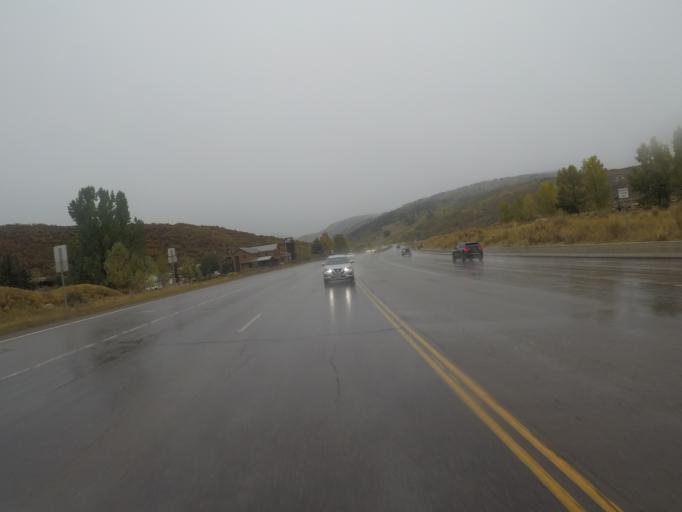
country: US
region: Colorado
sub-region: Pitkin County
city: Aspen
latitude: 39.2175
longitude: -106.8615
